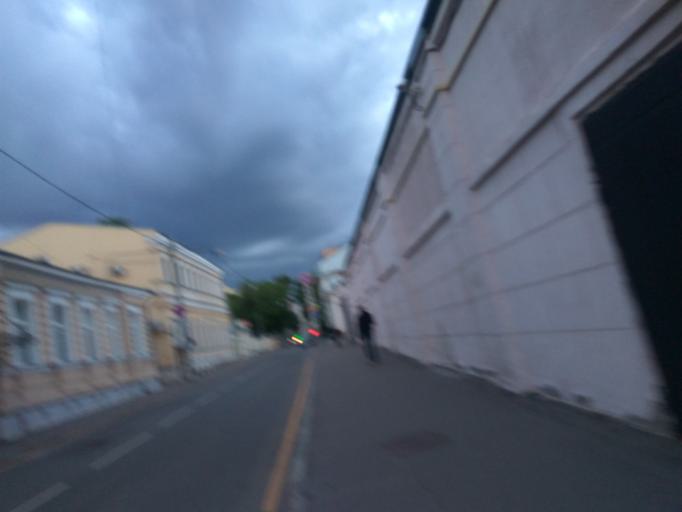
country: RU
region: Moskovskaya
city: Dorogomilovo
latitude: 55.7596
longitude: 37.5869
